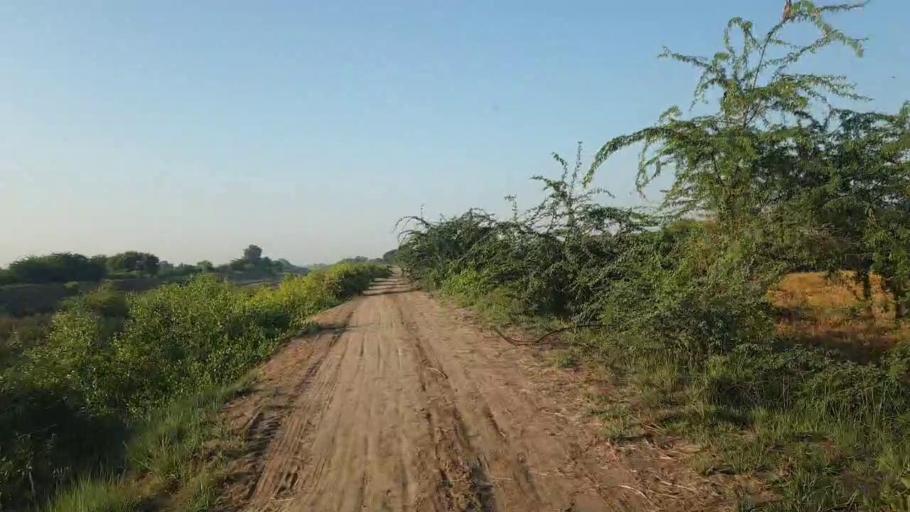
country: PK
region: Sindh
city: Badin
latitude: 24.6224
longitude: 68.7915
